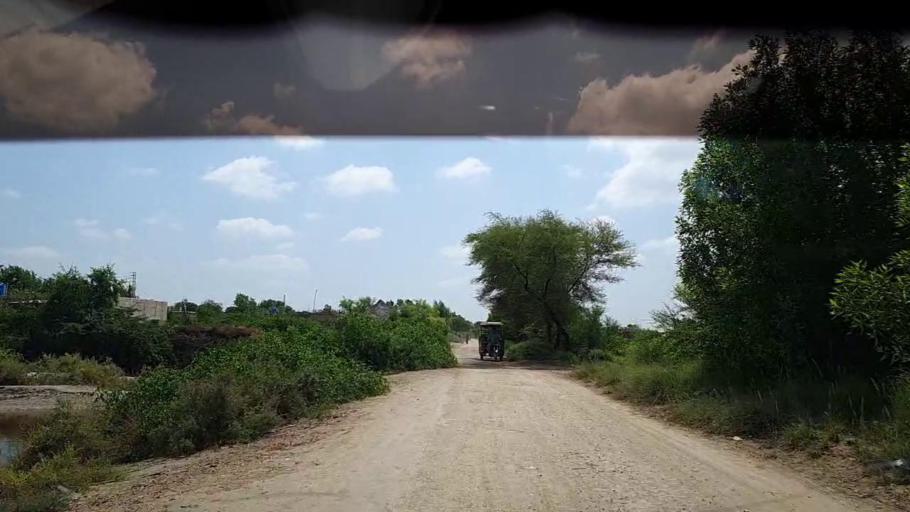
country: PK
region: Sindh
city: Kadhan
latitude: 24.5905
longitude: 68.9580
